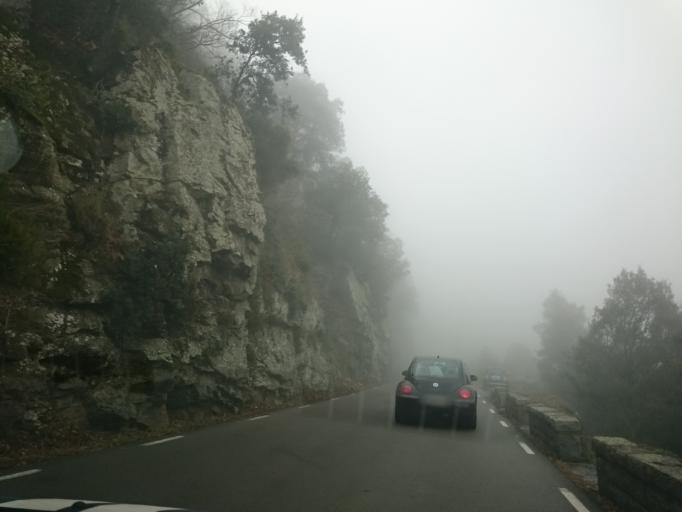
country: ES
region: Catalonia
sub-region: Provincia de Barcelona
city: Fogars de Montclus
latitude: 41.7569
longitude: 2.4700
